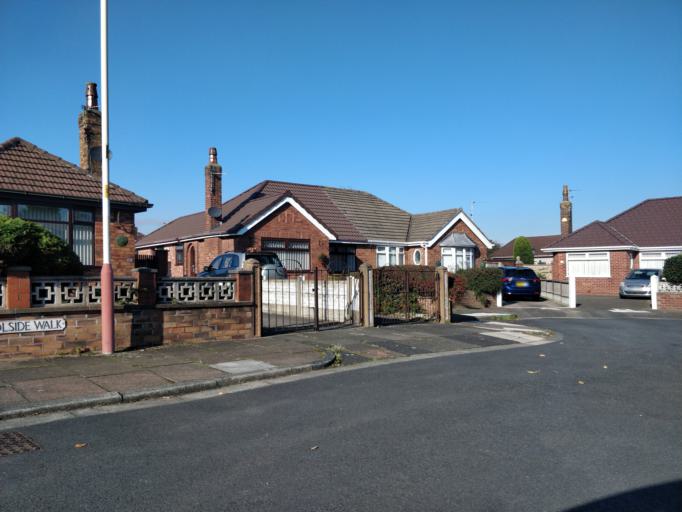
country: GB
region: England
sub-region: Lancashire
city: Banks
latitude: 53.6725
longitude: -2.9536
